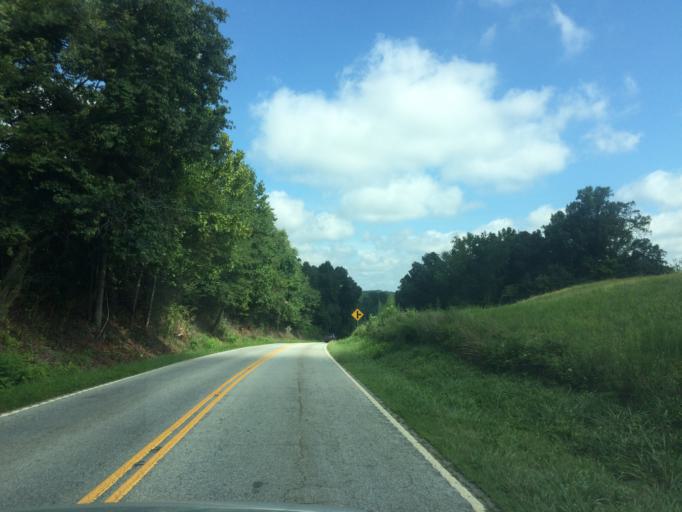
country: US
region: South Carolina
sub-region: Spartanburg County
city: Inman Mills
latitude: 35.0011
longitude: -82.1122
